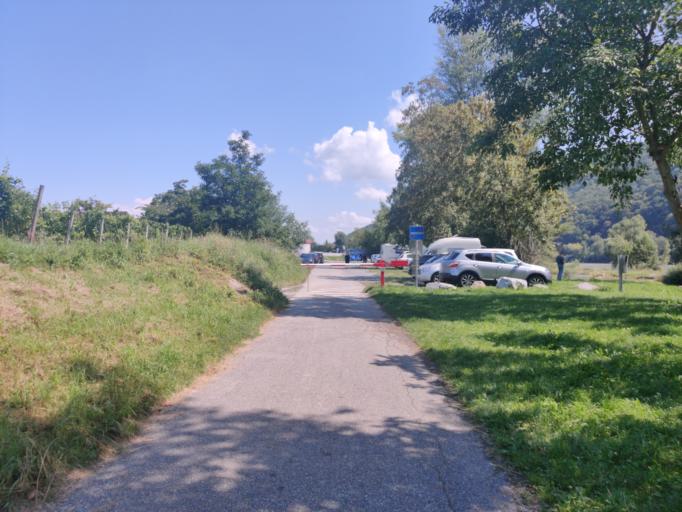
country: AT
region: Lower Austria
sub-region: Politischer Bezirk Krems
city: Durnstein
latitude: 48.3858
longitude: 15.5313
